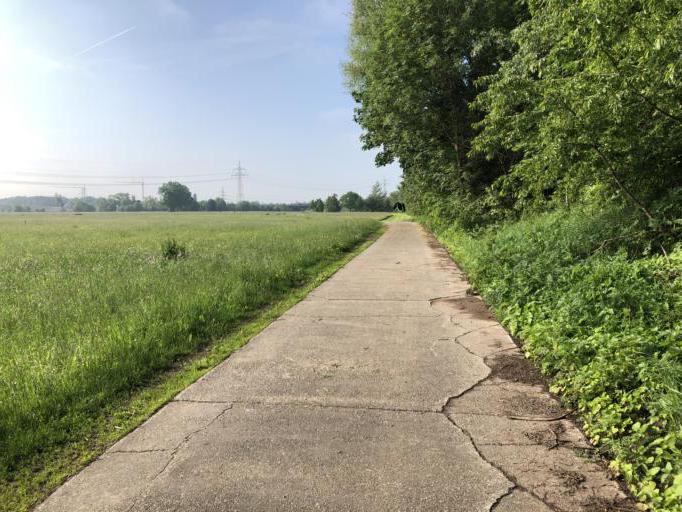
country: DE
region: Bavaria
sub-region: Regierungsbezirk Mittelfranken
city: Erlangen
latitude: 49.5659
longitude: 10.9780
